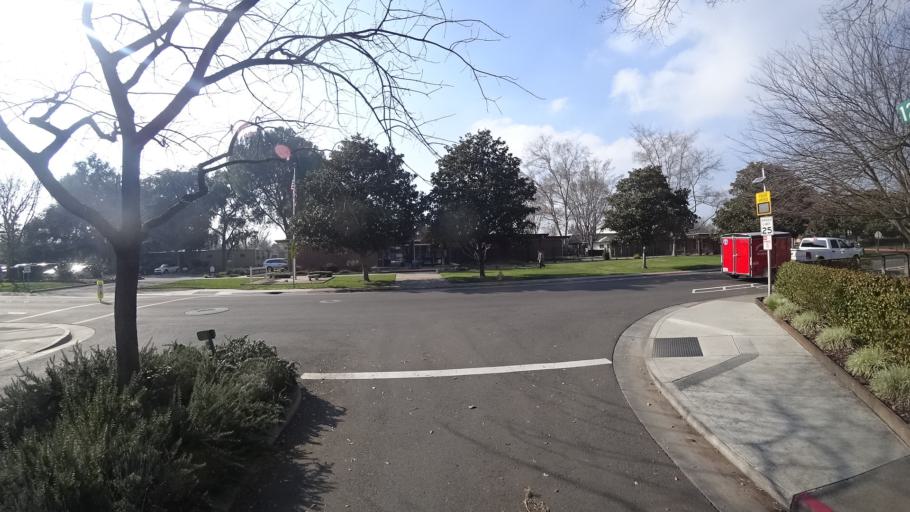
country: US
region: California
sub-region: Yolo County
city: Davis
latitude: 38.5544
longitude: -121.7468
